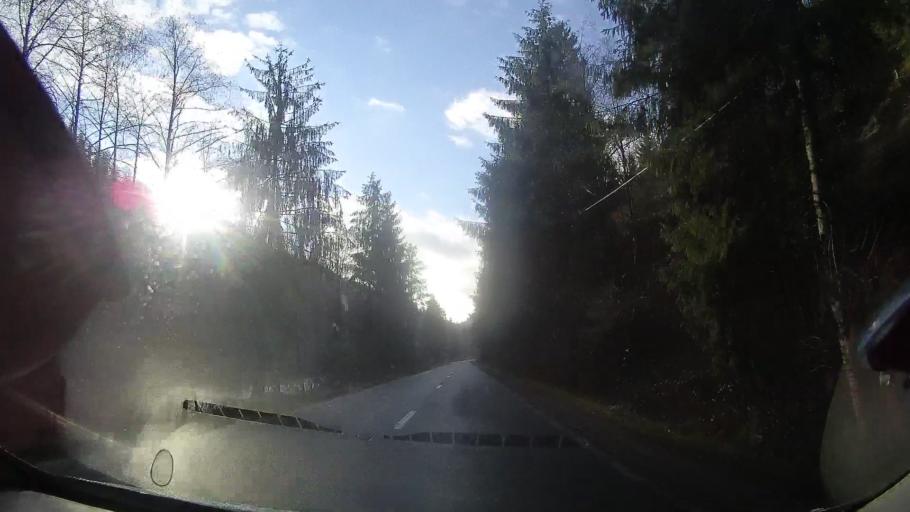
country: RO
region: Alba
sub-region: Comuna Albac
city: Albac
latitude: 46.4371
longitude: 22.9670
